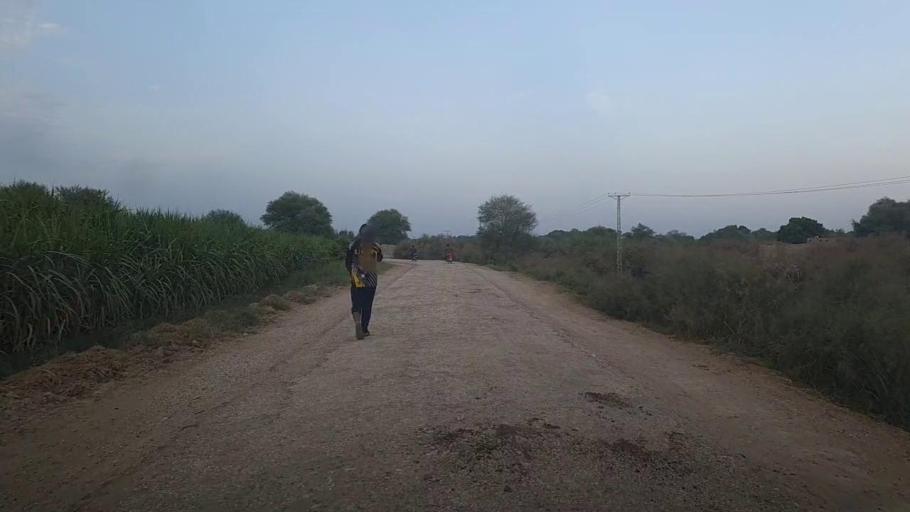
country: PK
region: Sindh
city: Kashmor
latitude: 28.3669
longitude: 69.7688
